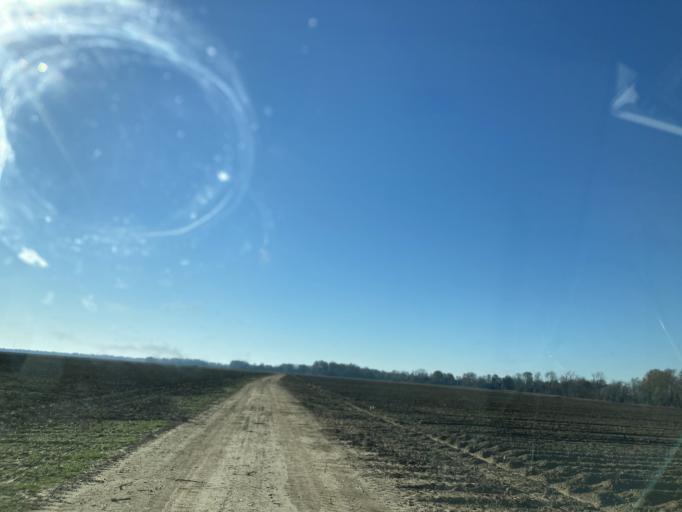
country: US
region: Mississippi
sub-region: Sharkey County
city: Rolling Fork
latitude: 32.8636
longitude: -90.6932
